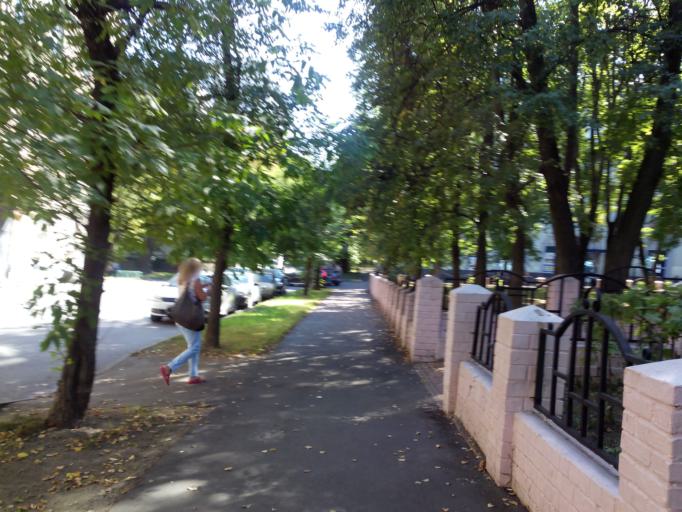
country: RU
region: Moskovskaya
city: Bol'shaya Setun'
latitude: 55.7334
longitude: 37.4182
